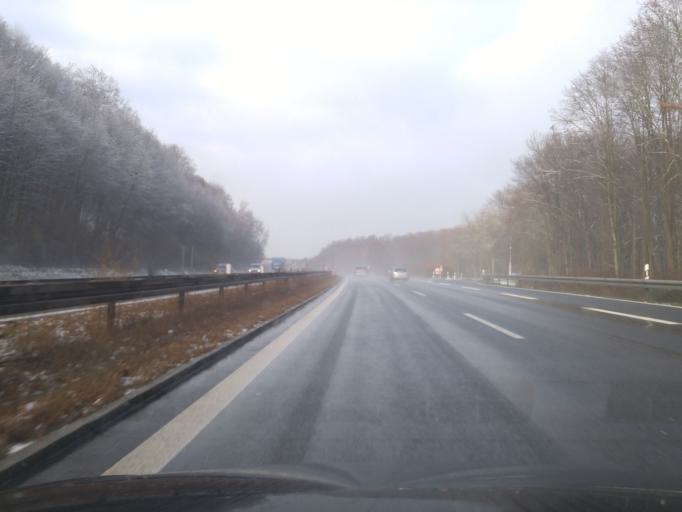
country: DE
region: Bavaria
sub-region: Regierungsbezirk Unterfranken
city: Fuchsstadt
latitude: 50.0967
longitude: 9.9804
